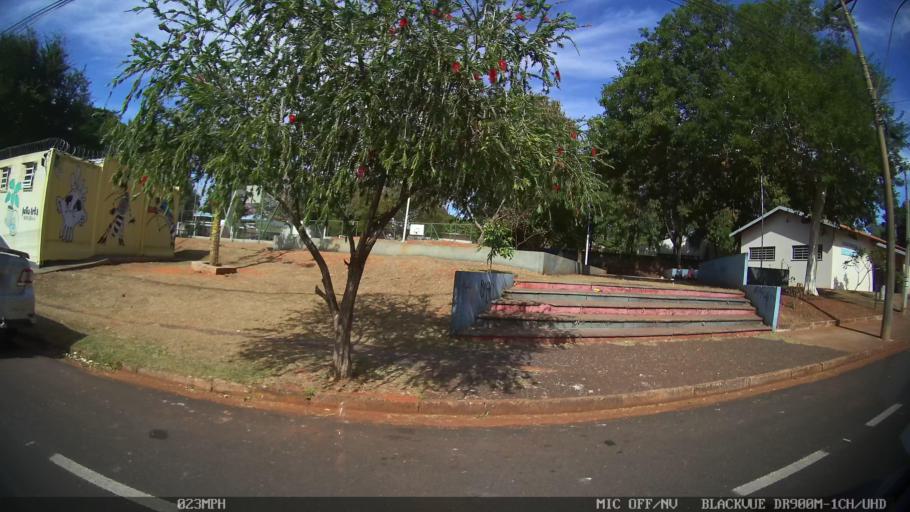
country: BR
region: Sao Paulo
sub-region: Sao Jose Do Rio Preto
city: Sao Jose do Rio Preto
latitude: -20.8441
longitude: -49.3456
